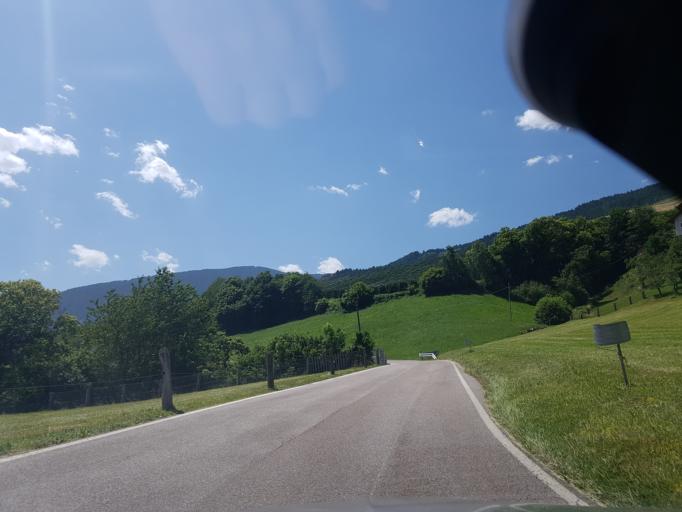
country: IT
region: Trentino-Alto Adige
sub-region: Bolzano
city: Villandro - Villanders
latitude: 46.6331
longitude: 11.5367
